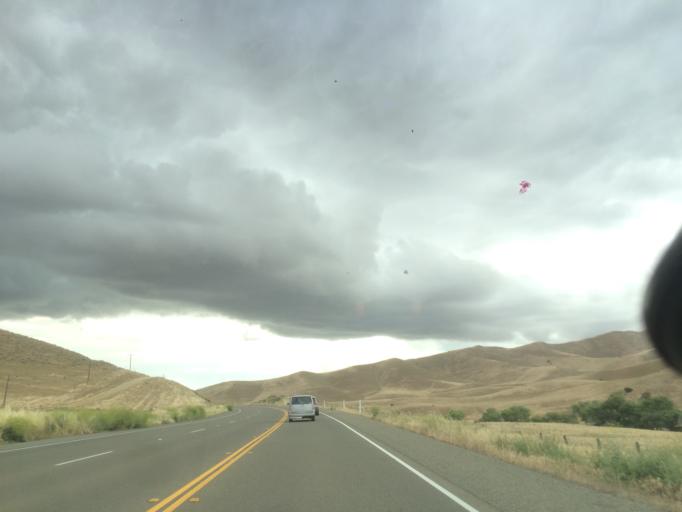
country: US
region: California
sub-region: Kings County
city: Avenal
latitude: 35.7748
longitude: -120.1463
